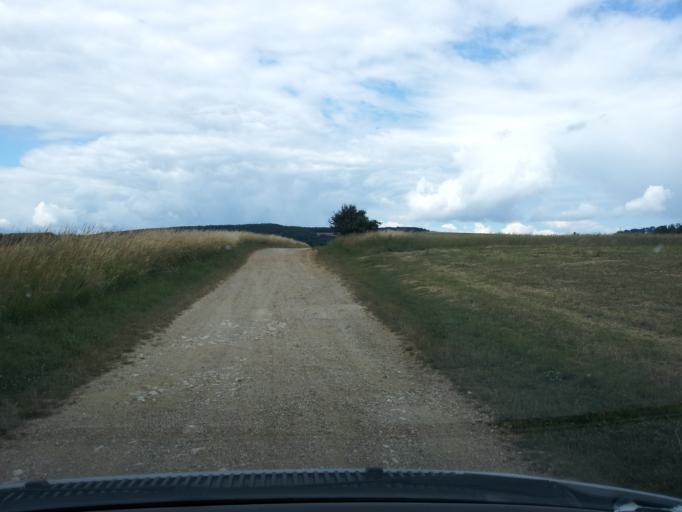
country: HU
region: Veszprem
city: Herend
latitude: 47.1838
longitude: 17.8022
